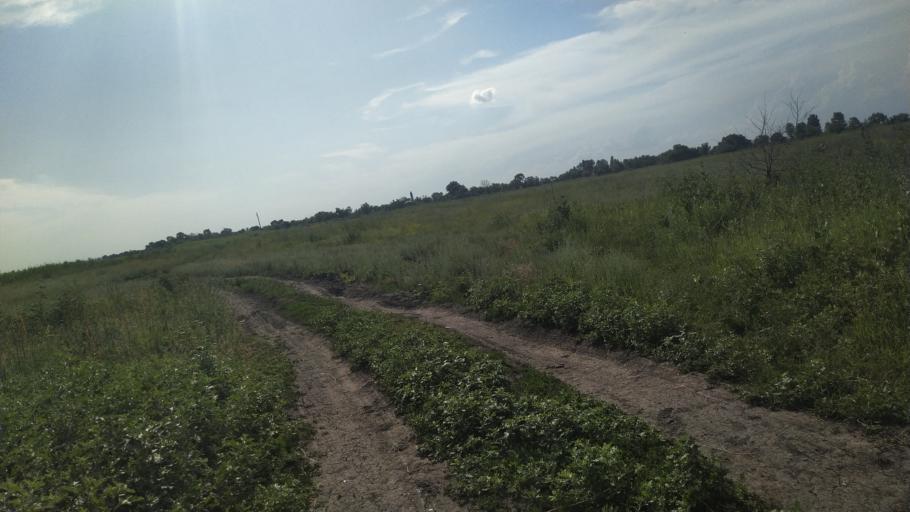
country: RU
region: Rostov
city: Kuleshovka
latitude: 47.1274
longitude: 39.6166
